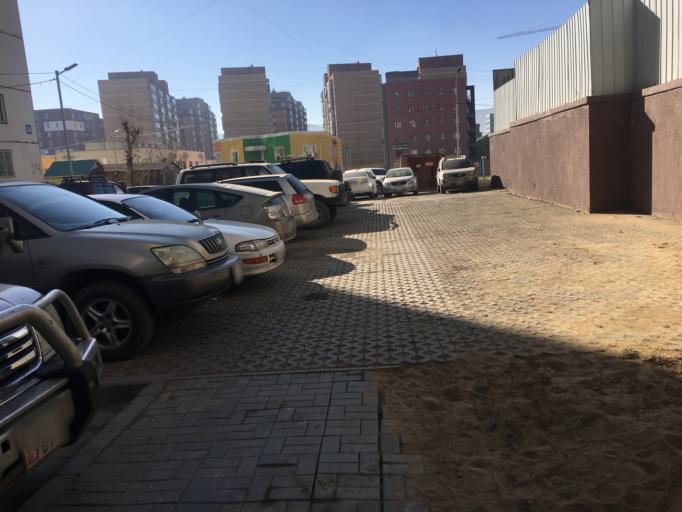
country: MN
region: Ulaanbaatar
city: Ulaanbaatar
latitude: 47.9215
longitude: 106.8880
